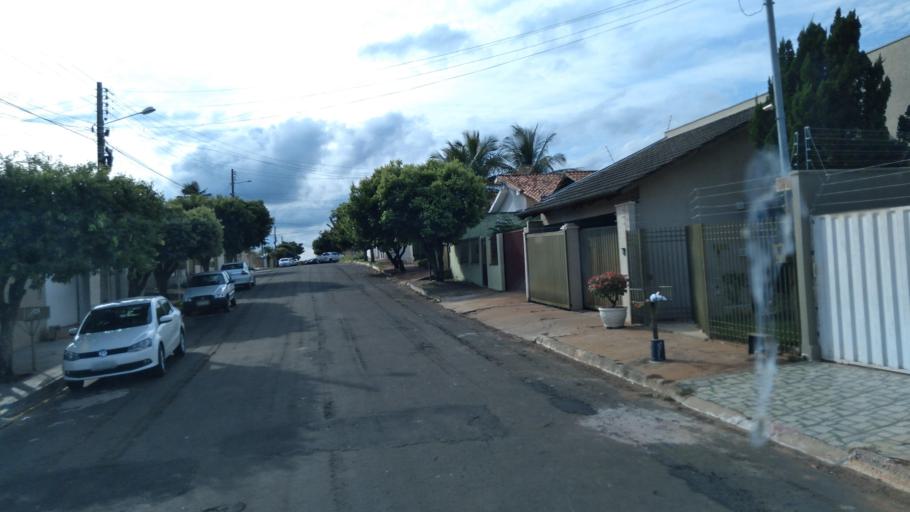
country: BR
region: Goias
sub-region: Mineiros
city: Mineiros
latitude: -17.5623
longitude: -52.5656
